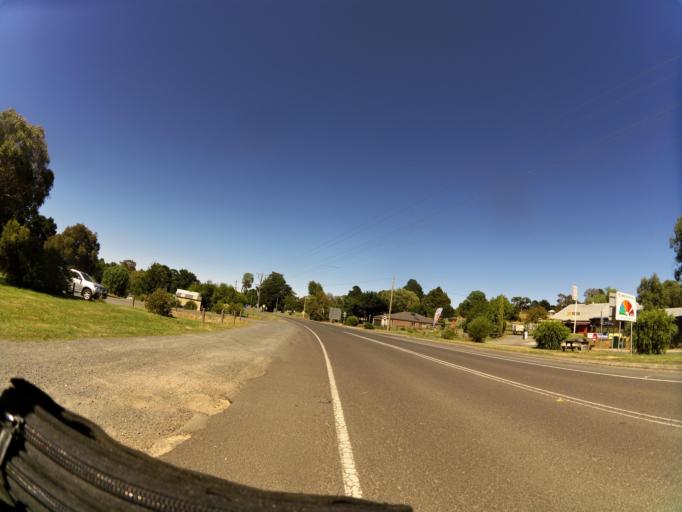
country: AU
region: Victoria
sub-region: Ballarat North
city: Delacombe
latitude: -37.6829
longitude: 143.5657
